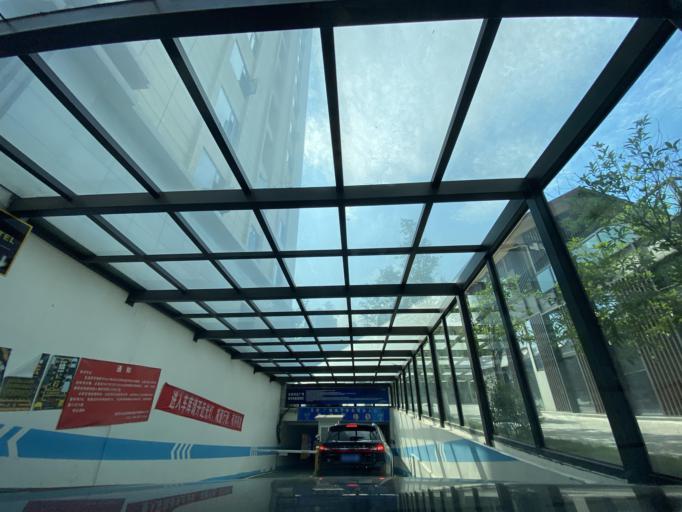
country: CN
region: Sichuan
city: Yanjiang
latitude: 30.1026
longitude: 104.6695
